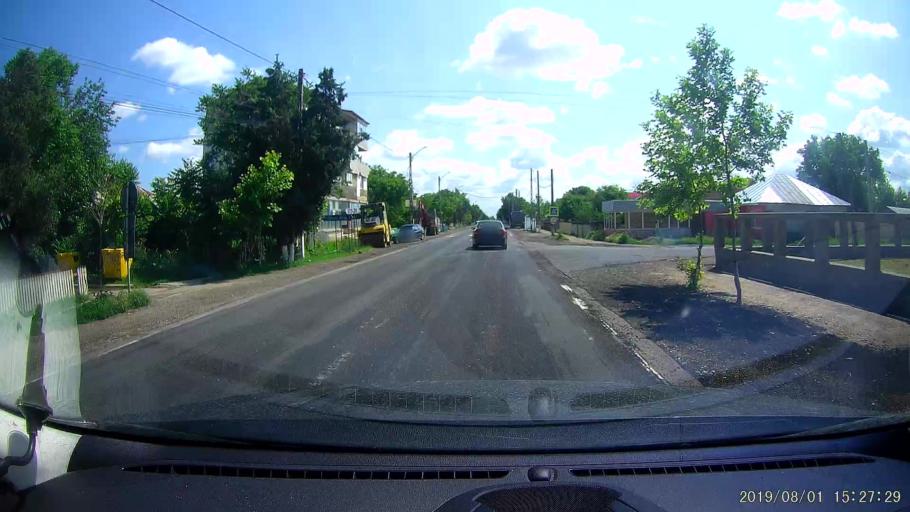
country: RO
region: Braila
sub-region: Comuna Viziru
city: Viziru
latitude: 45.0009
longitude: 27.7152
